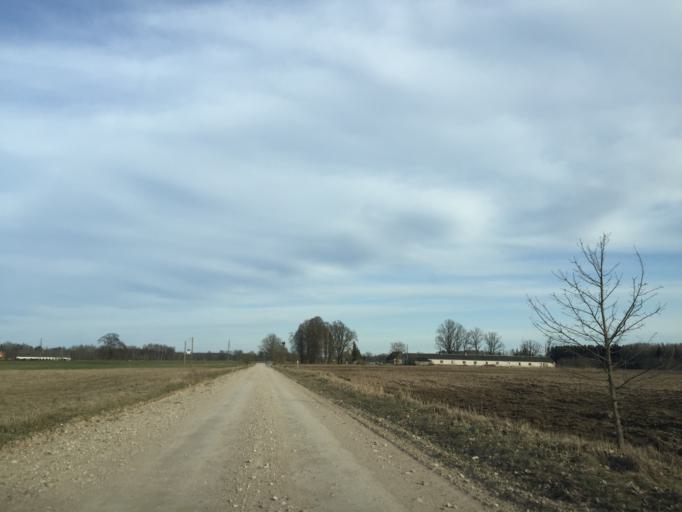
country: LV
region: Lielvarde
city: Lielvarde
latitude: 56.8024
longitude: 24.8001
